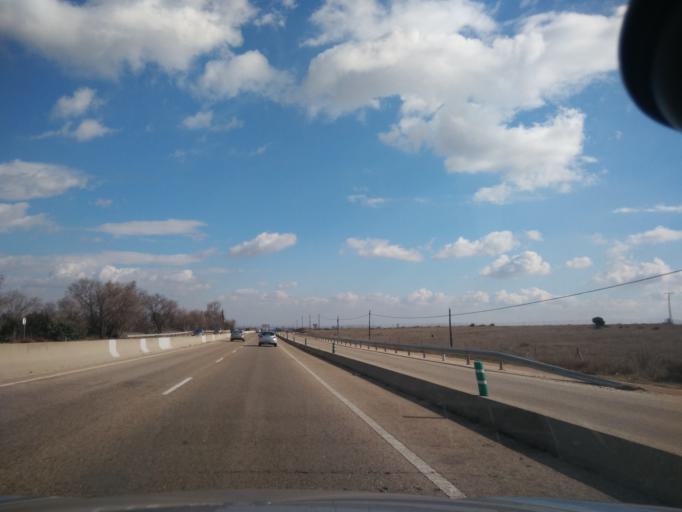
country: ES
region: Madrid
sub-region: Provincia de Madrid
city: Alcobendas
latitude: 40.5523
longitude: -3.6727
